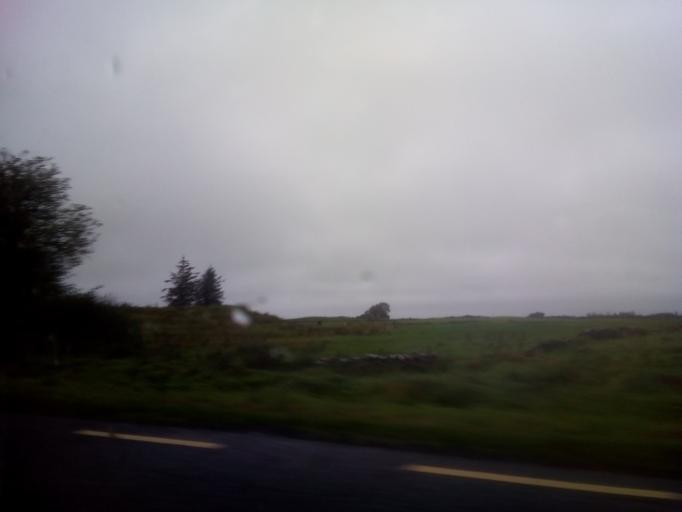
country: IE
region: Connaught
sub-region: Roscommon
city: Boyle
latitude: 53.8095
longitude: -8.3103
